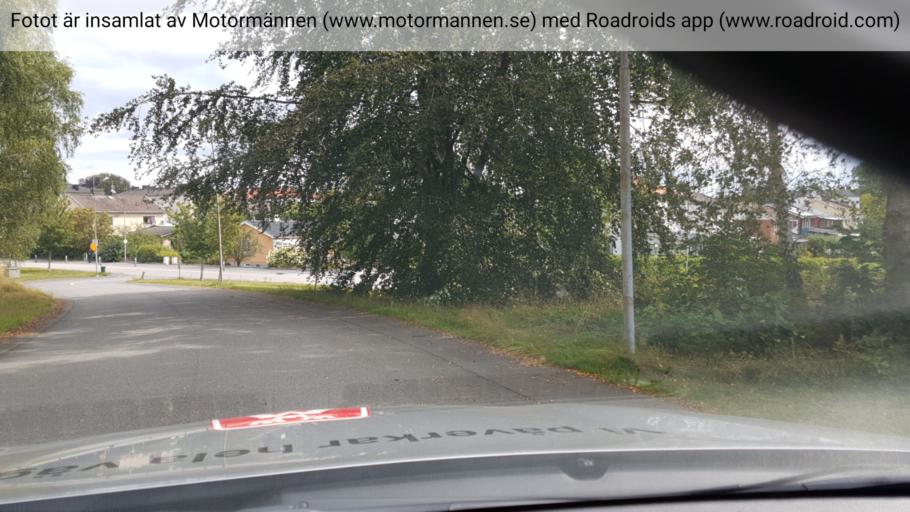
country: SE
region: Skane
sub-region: Hassleholms Kommun
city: Hassleholm
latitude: 56.1525
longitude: 13.7637
